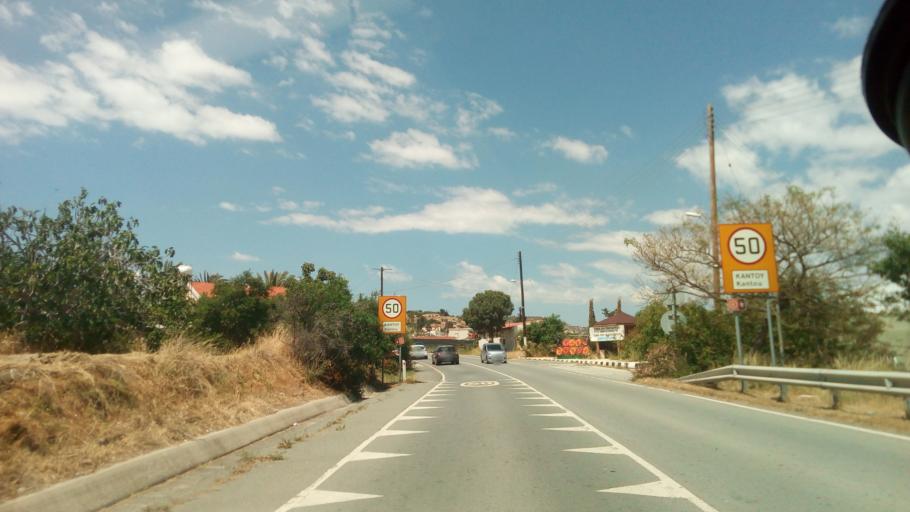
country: CY
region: Limassol
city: Erimi
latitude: 34.6878
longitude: 32.9091
